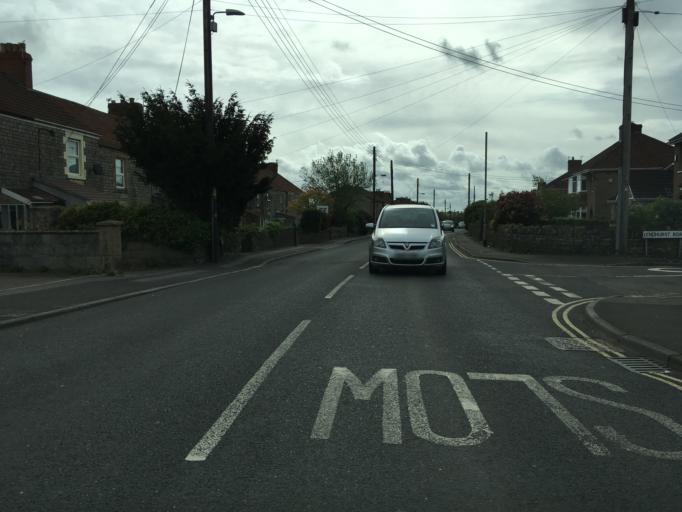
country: GB
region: England
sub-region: Bath and North East Somerset
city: Midsomer Norton
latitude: 51.2807
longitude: -2.4786
